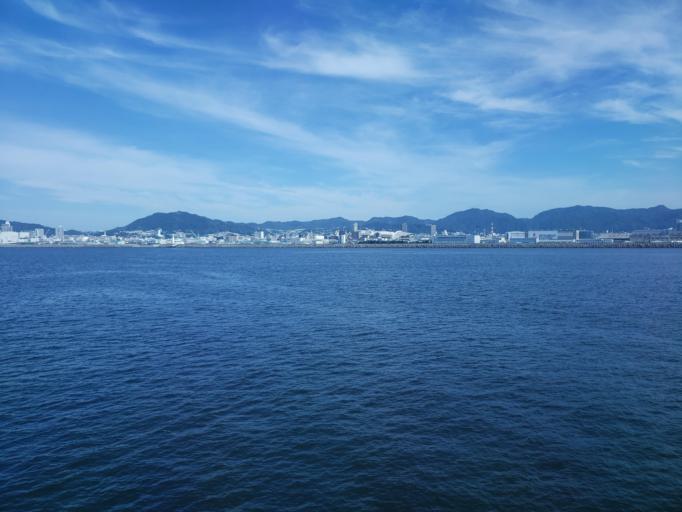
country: JP
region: Hyogo
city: Kobe
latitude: 34.6406
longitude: 135.1785
